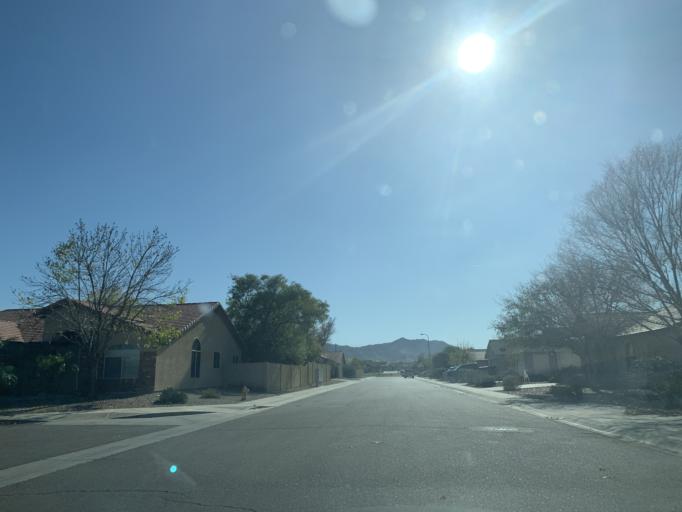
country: US
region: Arizona
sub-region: Maricopa County
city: Laveen
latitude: 33.3959
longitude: -112.1235
